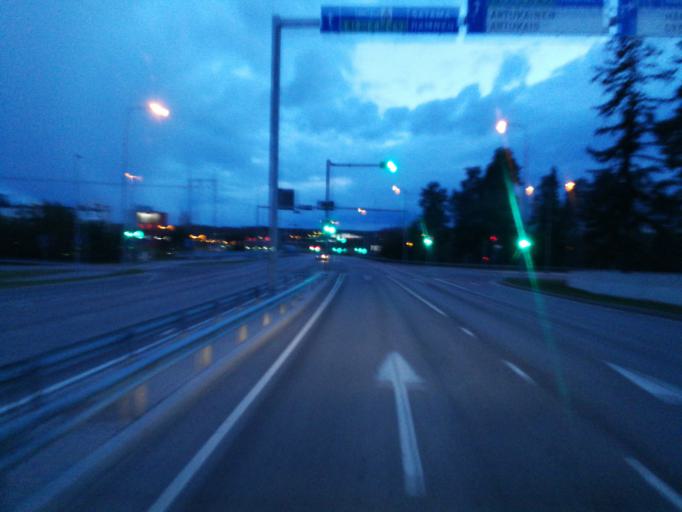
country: FI
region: Varsinais-Suomi
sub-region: Turku
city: Raisio
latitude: 60.4624
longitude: 22.2000
